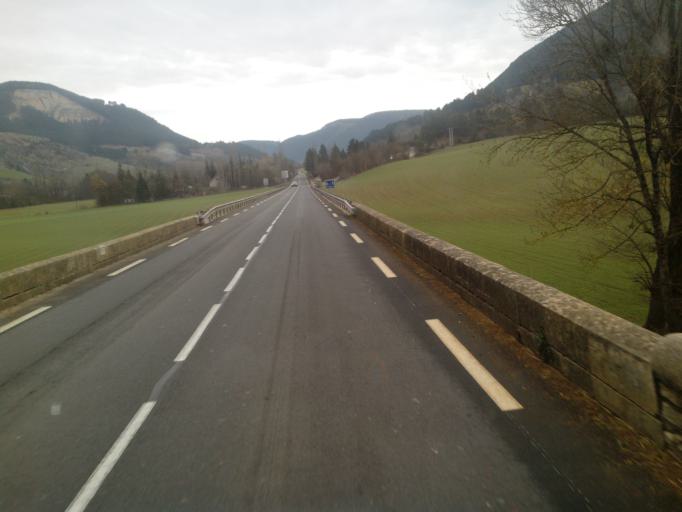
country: FR
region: Languedoc-Roussillon
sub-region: Departement de la Lozere
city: Mende
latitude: 44.4771
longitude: 3.4972
